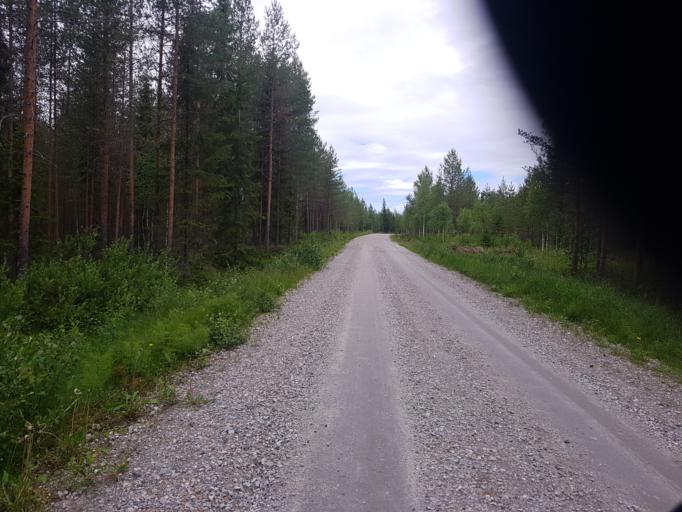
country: FI
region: Kainuu
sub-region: Kehys-Kainuu
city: Kuhmo
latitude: 64.4323
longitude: 29.5793
